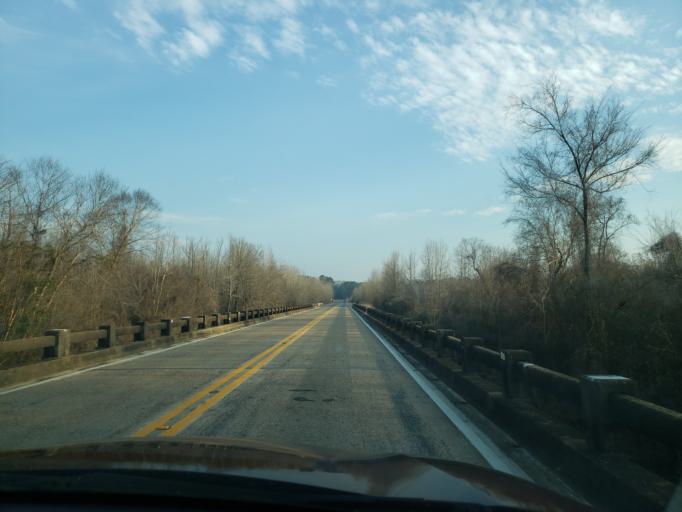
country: US
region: Alabama
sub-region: Hale County
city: Greensboro
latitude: 32.8302
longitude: -87.6045
